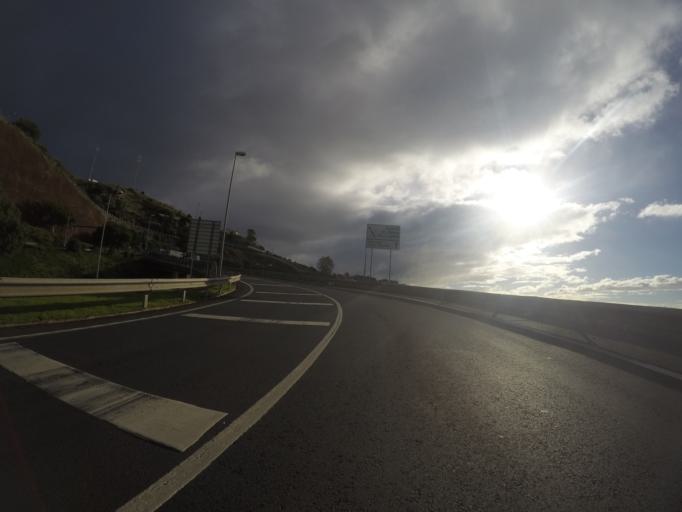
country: PT
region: Madeira
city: Canico
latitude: 32.6466
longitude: -16.8656
